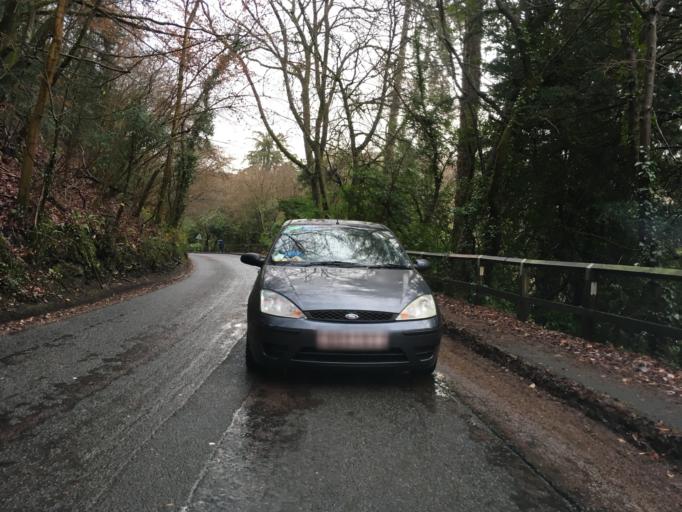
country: GB
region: England
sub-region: Gloucestershire
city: Minchinhampton
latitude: 51.6915
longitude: -2.1967
